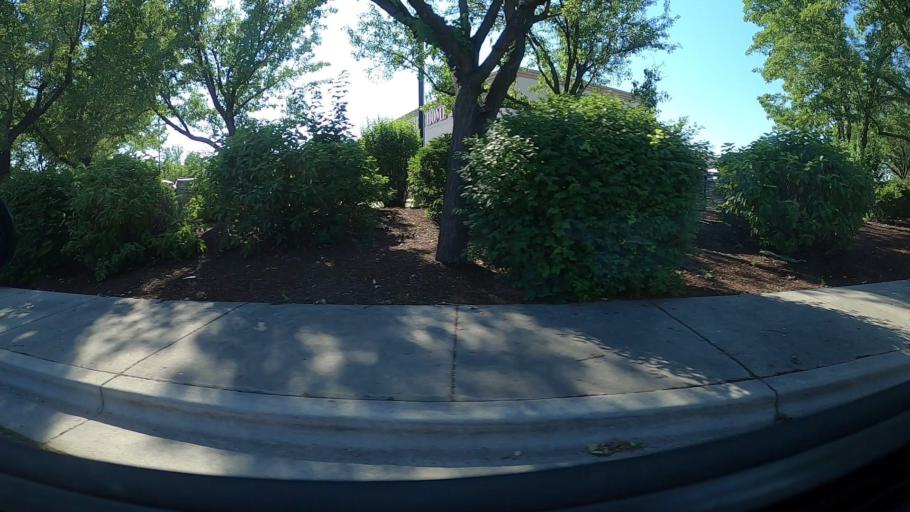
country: US
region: Idaho
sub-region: Ada County
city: Meridian
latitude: 43.5943
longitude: -116.3884
